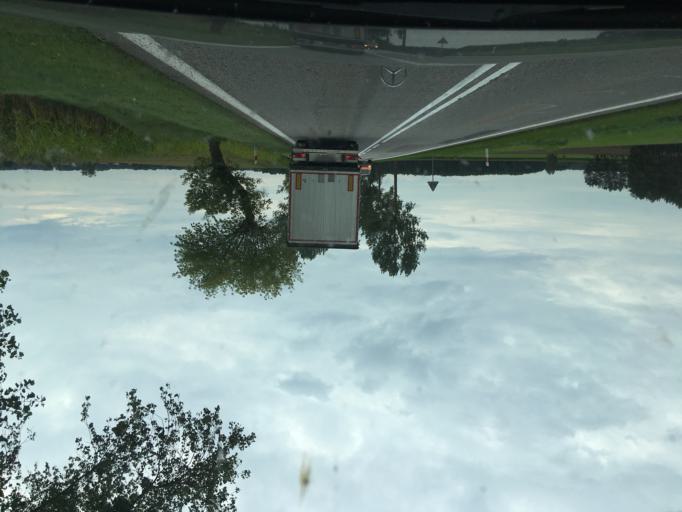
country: PL
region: Podlasie
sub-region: Powiat kolnenski
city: Stawiski
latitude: 53.3203
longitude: 22.1522
